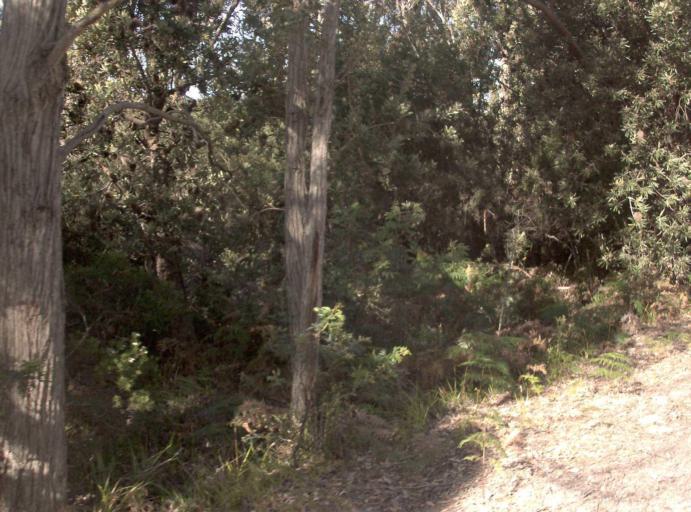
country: AU
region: Victoria
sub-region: East Gippsland
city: Lakes Entrance
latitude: -37.7982
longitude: 148.6818
